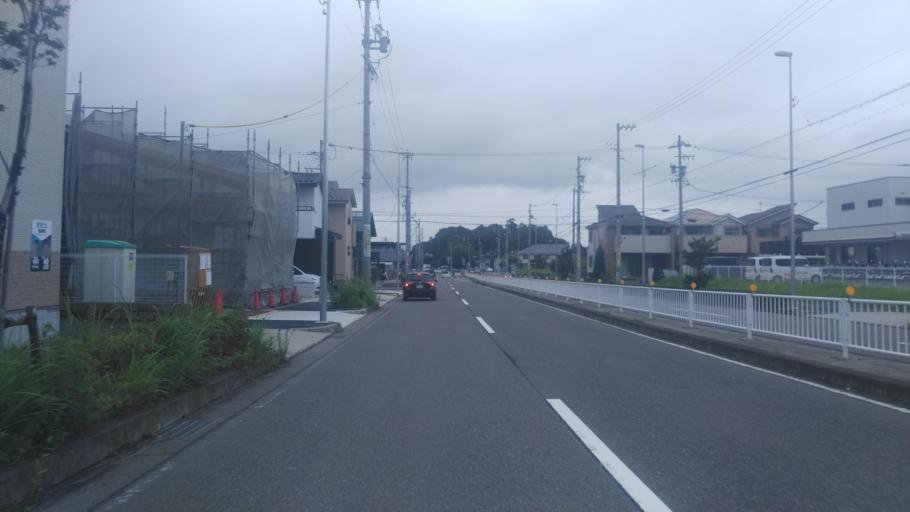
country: JP
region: Aichi
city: Kasugai
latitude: 35.2498
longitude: 137.0369
